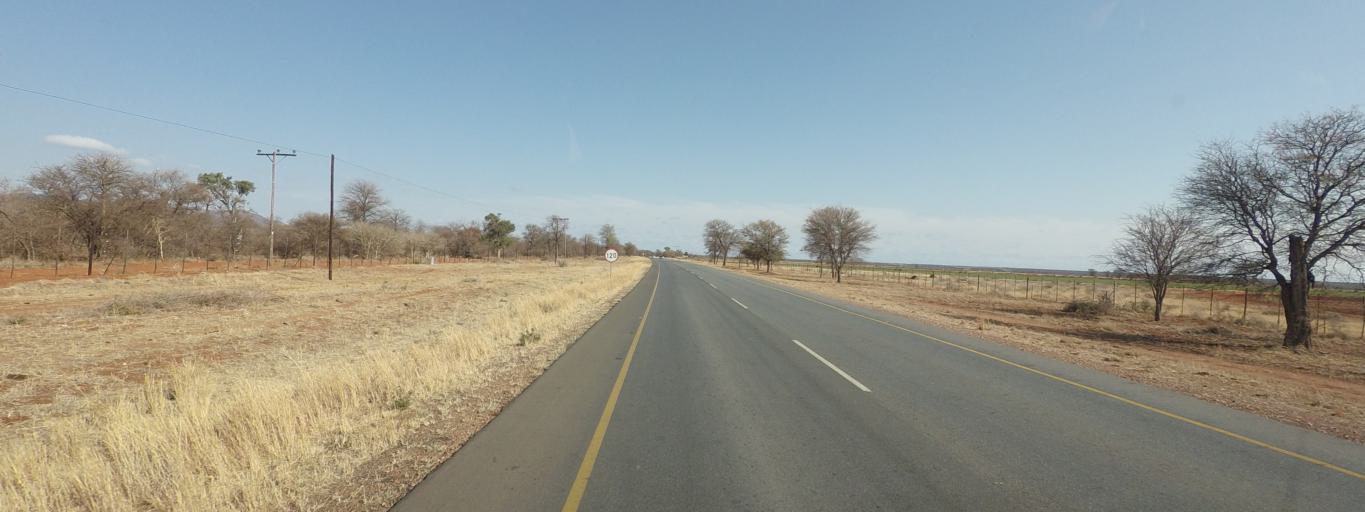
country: BW
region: Central
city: Makobeng
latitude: -22.9839
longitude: 27.9220
